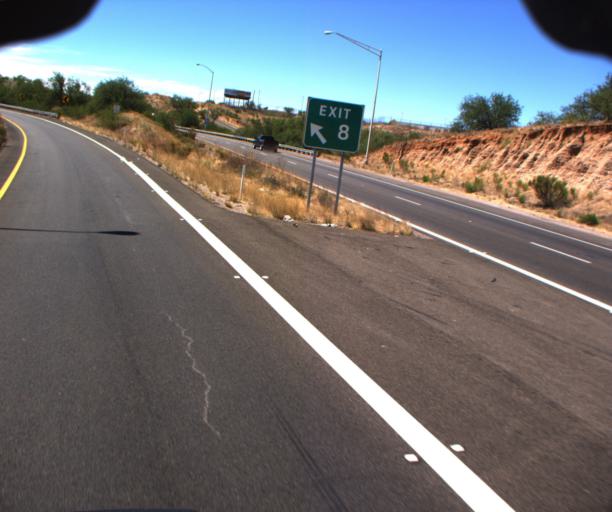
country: US
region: Arizona
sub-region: Santa Cruz County
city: Nogales
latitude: 31.3980
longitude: -110.9613
